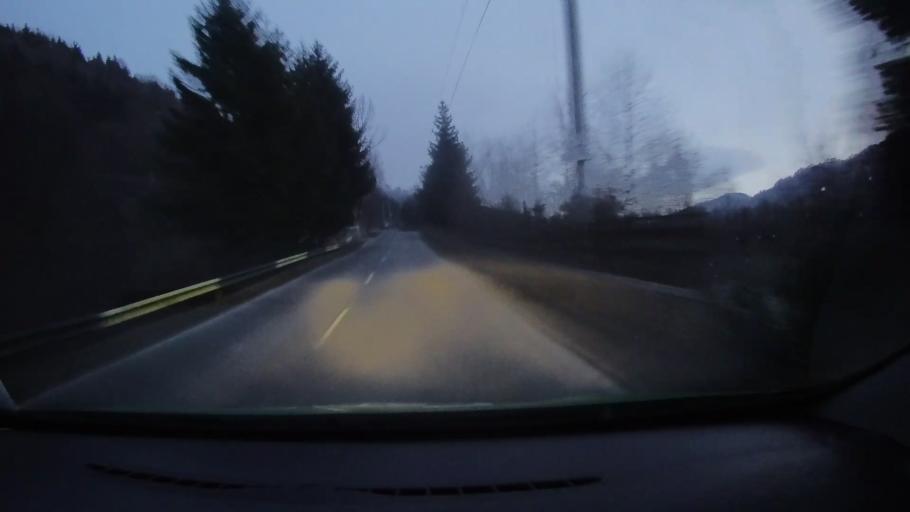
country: RO
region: Prahova
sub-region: Comuna Valea Doftanei
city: Tesila
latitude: 45.2779
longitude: 25.7292
